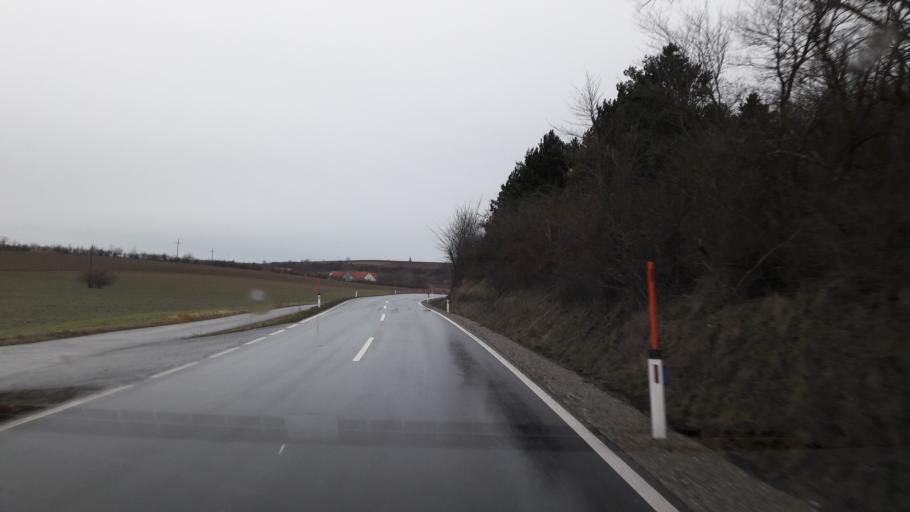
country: AT
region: Lower Austria
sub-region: Politischer Bezirk Mistelbach
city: Hochleithen
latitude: 48.4363
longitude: 16.5427
